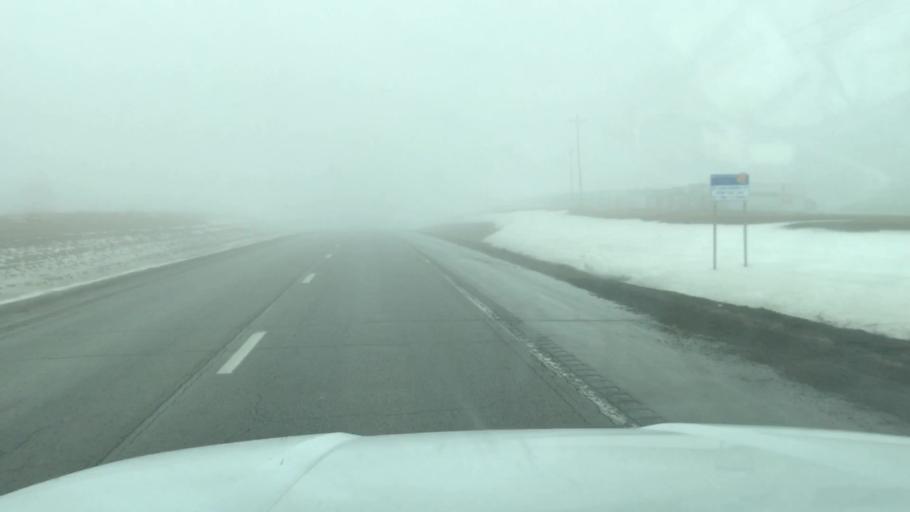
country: US
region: Missouri
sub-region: Clinton County
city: Cameron
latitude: 39.7550
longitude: -94.3006
